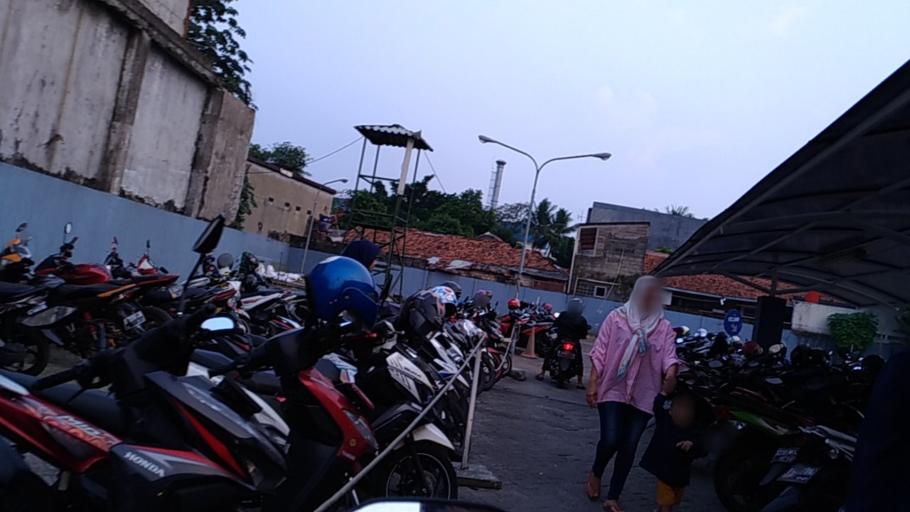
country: ID
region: West Java
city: Depok
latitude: -6.3719
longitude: 106.8604
